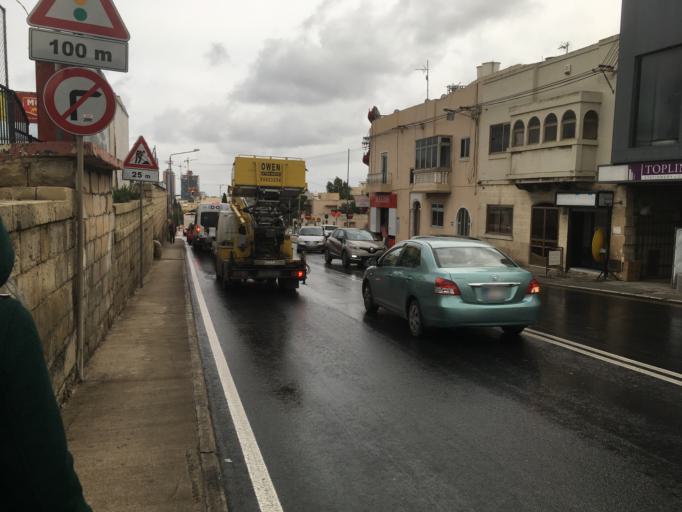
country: MT
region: Is-Swieqi
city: Swieqi
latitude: 35.9236
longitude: 14.4762
